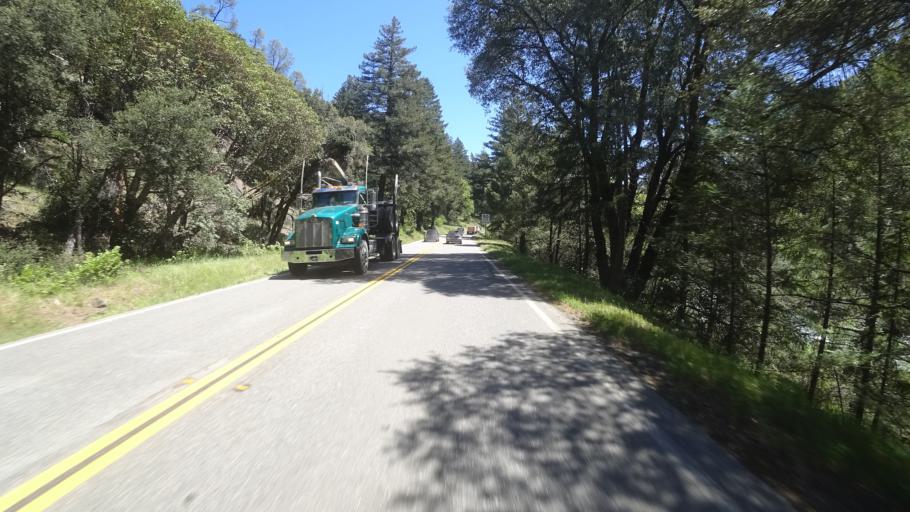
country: US
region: California
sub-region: Trinity County
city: Hayfork
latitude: 40.7498
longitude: -123.2759
